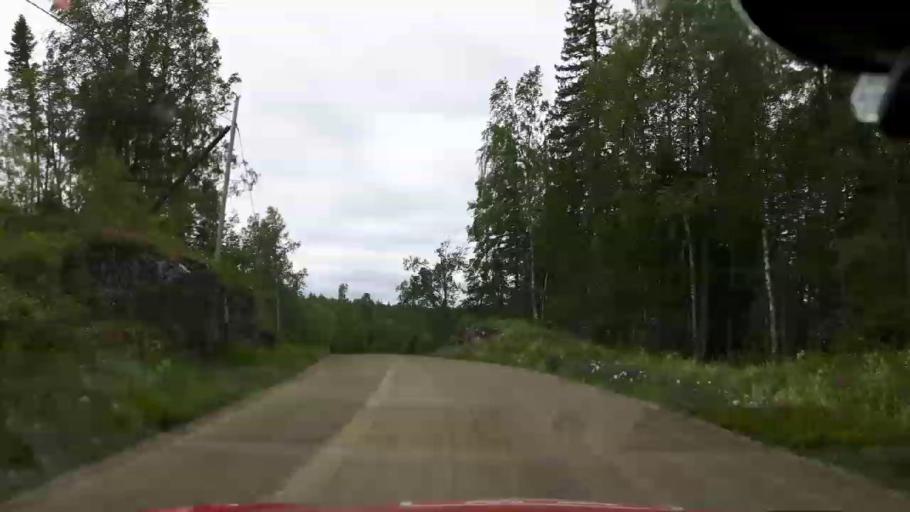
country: SE
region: Jaemtland
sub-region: OEstersunds Kommun
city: Brunflo
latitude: 62.9055
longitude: 15.1061
